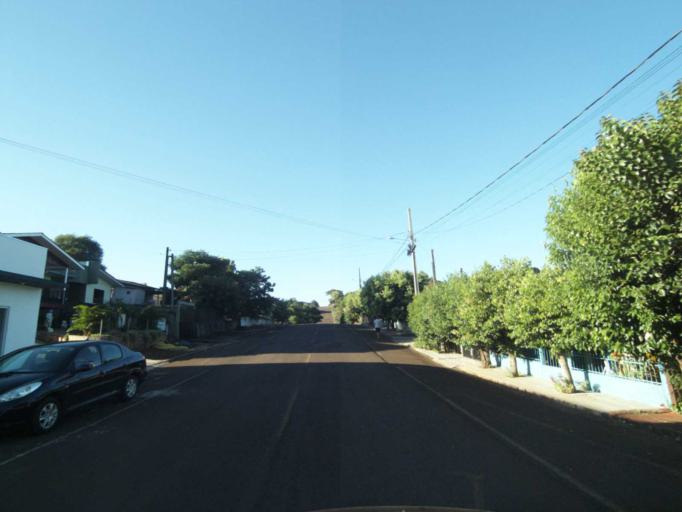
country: BR
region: Parana
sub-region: Coronel Vivida
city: Coronel Vivida
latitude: -25.9653
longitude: -52.8125
